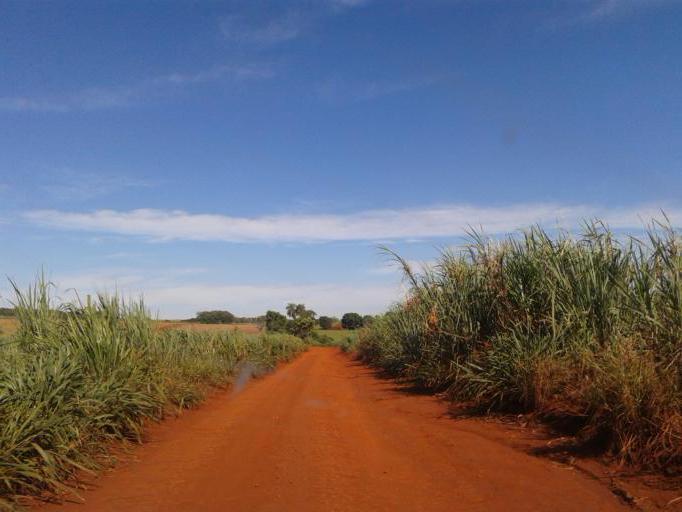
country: BR
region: Minas Gerais
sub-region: Capinopolis
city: Capinopolis
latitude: -18.6779
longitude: -49.6341
